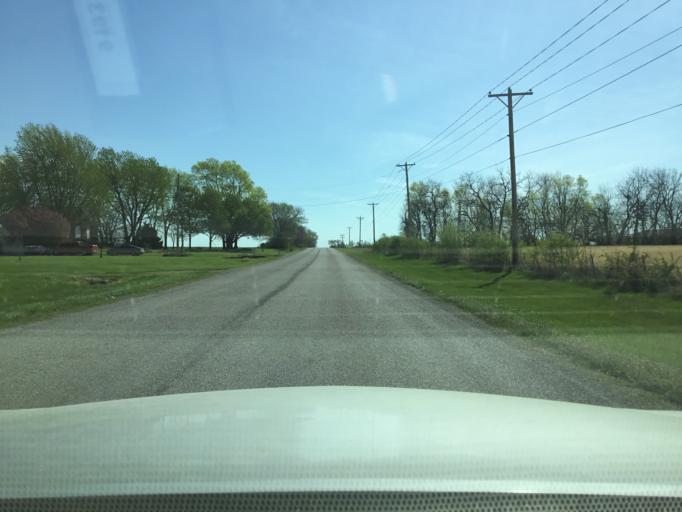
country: US
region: Kansas
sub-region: Neosho County
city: Chanute
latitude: 37.6458
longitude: -95.4494
